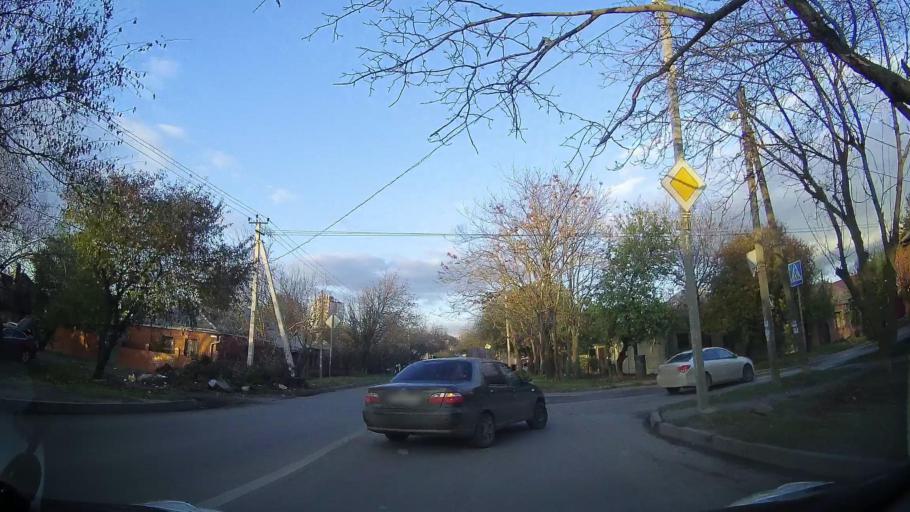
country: RU
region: Rostov
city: Imeni Chkalova
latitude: 47.2703
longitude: 39.7797
